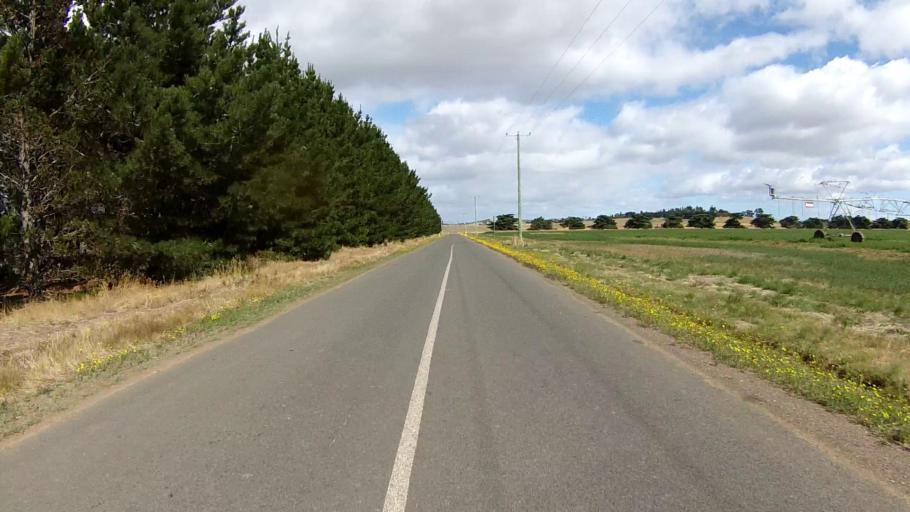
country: AU
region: Tasmania
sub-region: Northern Midlands
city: Evandale
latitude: -41.7770
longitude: 147.4722
